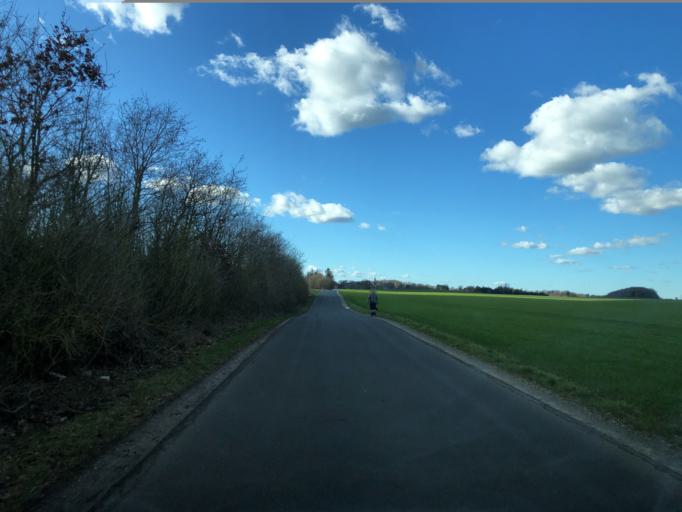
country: DK
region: Central Jutland
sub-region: Favrskov Kommune
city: Hammel
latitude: 56.2964
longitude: 9.9453
